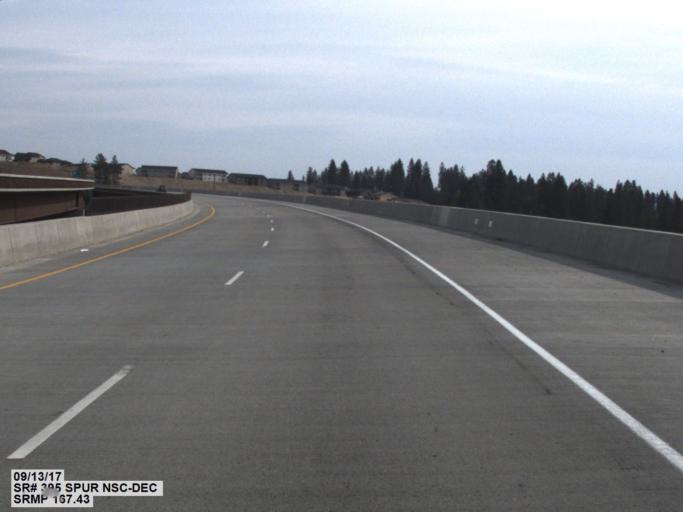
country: US
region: Washington
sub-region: Spokane County
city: Fairwood
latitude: 47.7807
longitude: -117.4025
